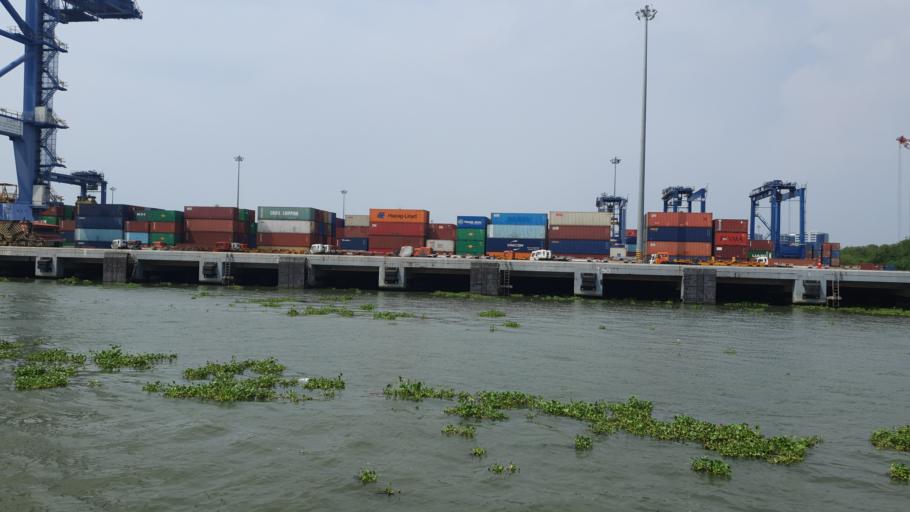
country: IN
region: Kerala
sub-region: Ernakulam
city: Cochin
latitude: 9.9779
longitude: 76.2542
